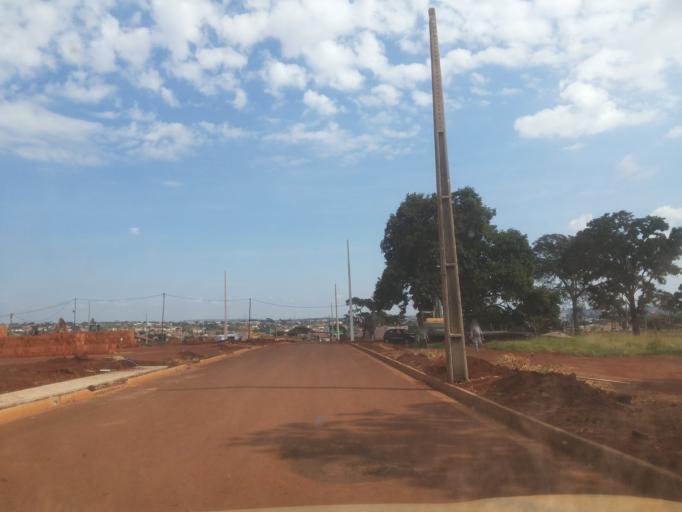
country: BR
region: Minas Gerais
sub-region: Ituiutaba
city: Ituiutaba
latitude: -18.9756
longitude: -49.4376
